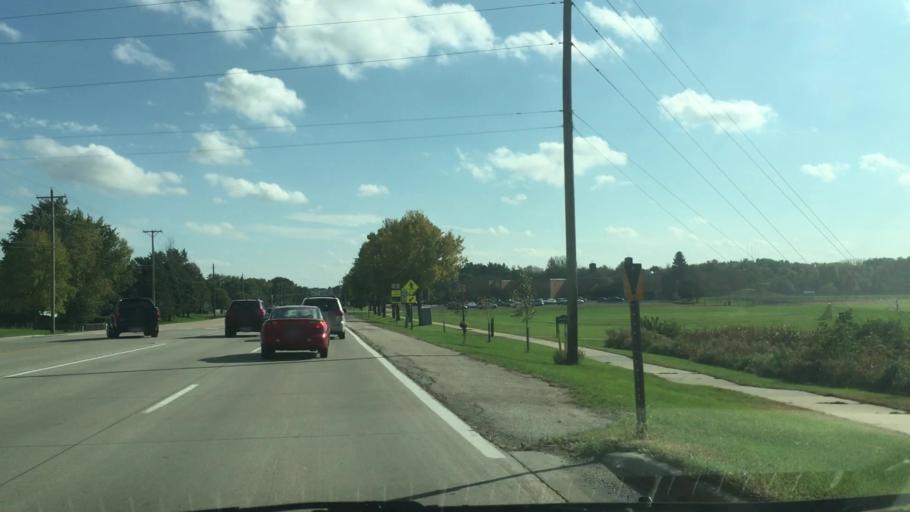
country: US
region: Minnesota
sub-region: Olmsted County
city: Rochester
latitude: 43.9898
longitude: -92.4422
